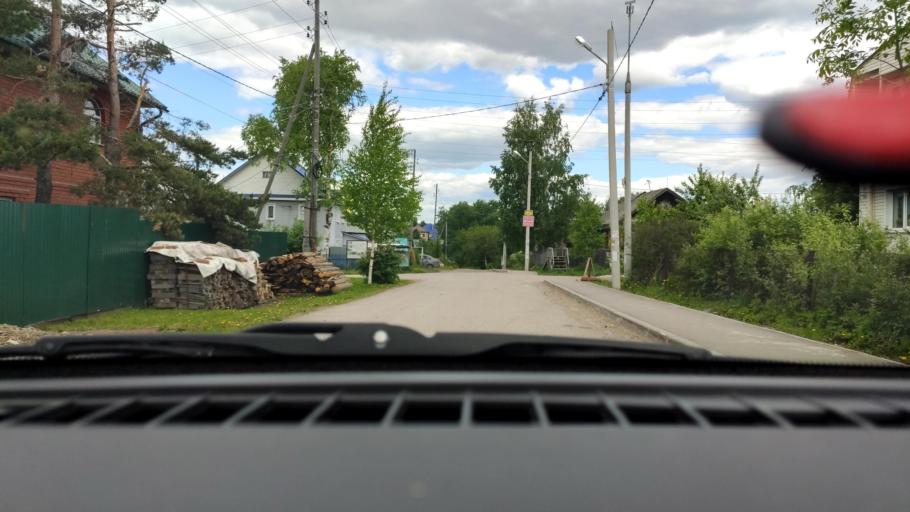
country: RU
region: Perm
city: Perm
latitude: 58.0461
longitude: 56.3585
